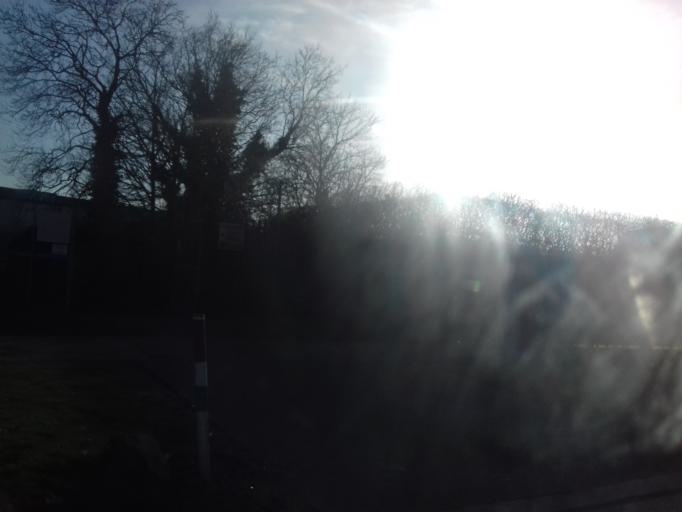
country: IE
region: Leinster
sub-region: Fingal County
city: Blanchardstown
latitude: 53.4060
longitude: -6.3638
